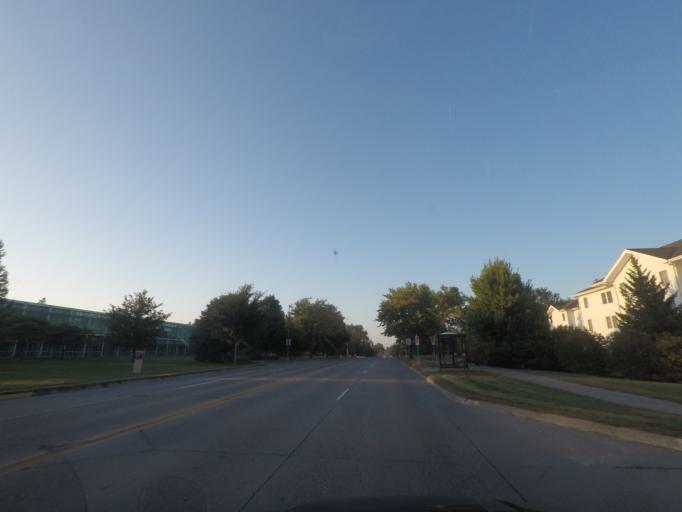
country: US
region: Iowa
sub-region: Story County
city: Ames
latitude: 42.0340
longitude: -93.6447
